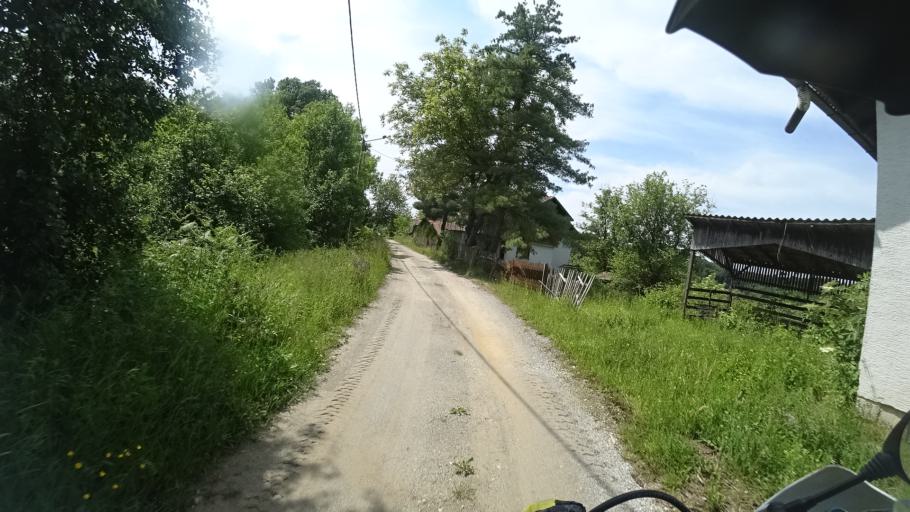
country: HR
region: Sisacko-Moslavacka
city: Gvozd
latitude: 45.3819
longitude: 15.8541
